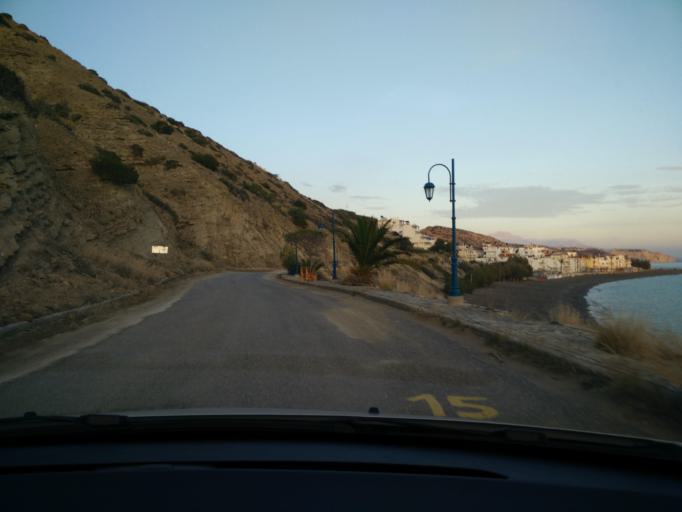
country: GR
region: Crete
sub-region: Nomos Lasithiou
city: Gra Liyia
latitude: 35.0028
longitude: 25.5797
